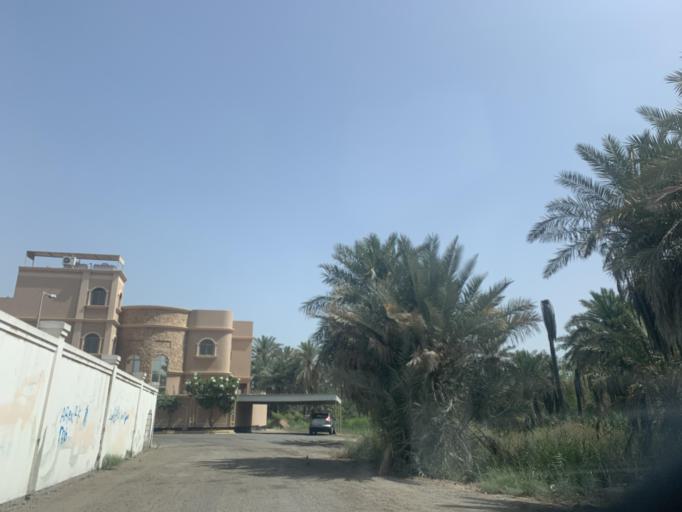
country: BH
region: Manama
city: Jidd Hafs
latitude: 26.2024
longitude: 50.5561
